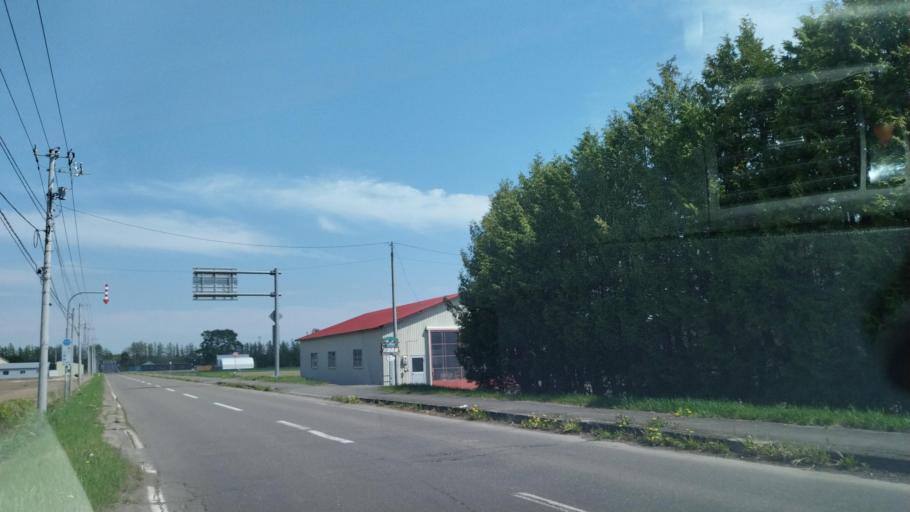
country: JP
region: Hokkaido
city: Otofuke
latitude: 43.1020
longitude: 143.2145
